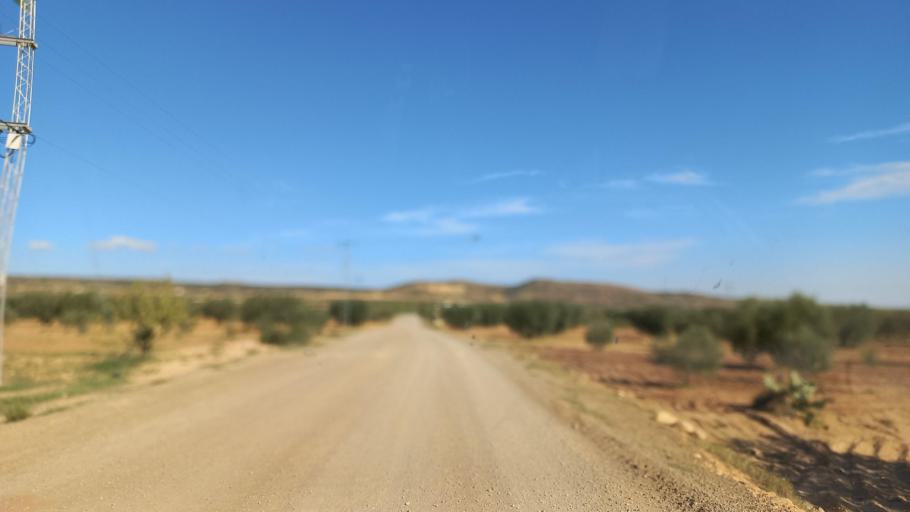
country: TN
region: Al Qasrayn
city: Sbiba
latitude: 35.2959
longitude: 9.1028
